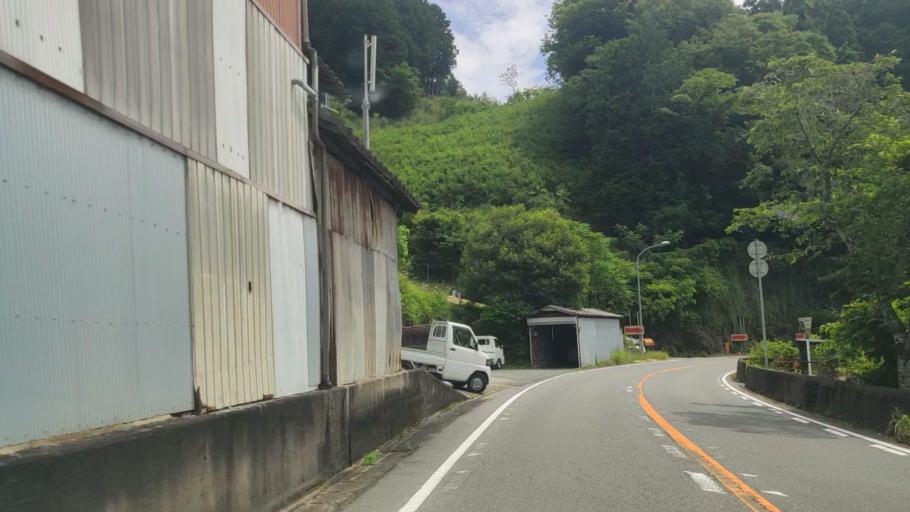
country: JP
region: Hyogo
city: Yamazakicho-nakabirose
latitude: 35.0747
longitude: 134.3595
